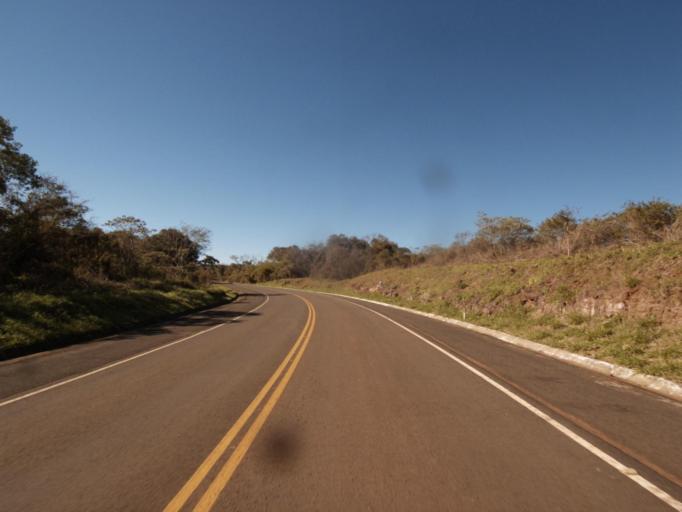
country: AR
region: Misiones
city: Bernardo de Irigoyen
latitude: -26.6134
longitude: -53.6963
